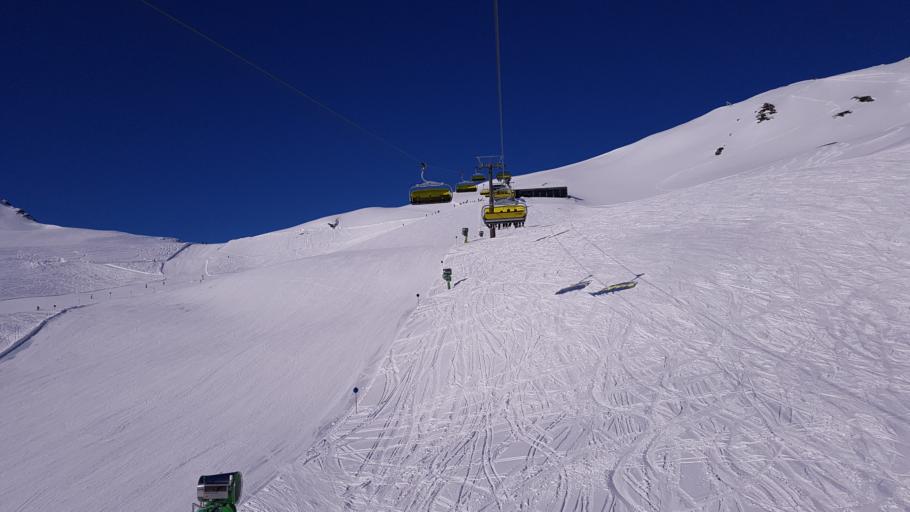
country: AT
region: Salzburg
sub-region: Politischer Bezirk Zell am See
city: Neukirchen am Grossvenediger
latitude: 47.2942
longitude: 12.2721
